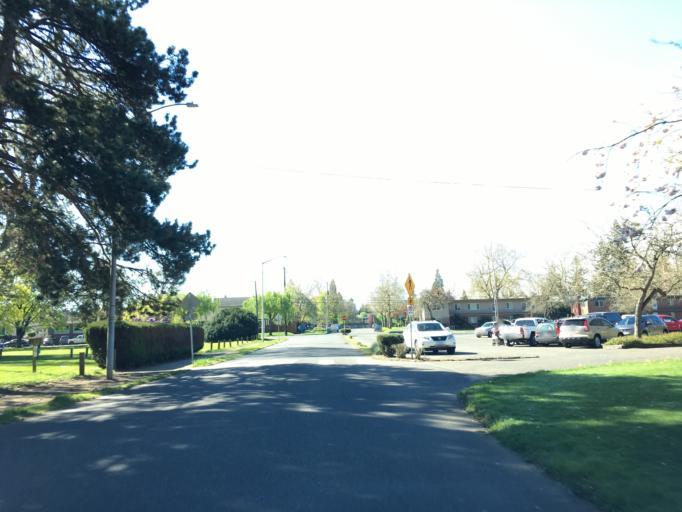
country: US
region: Oregon
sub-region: Multnomah County
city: Lents
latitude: 45.5382
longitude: -122.5895
